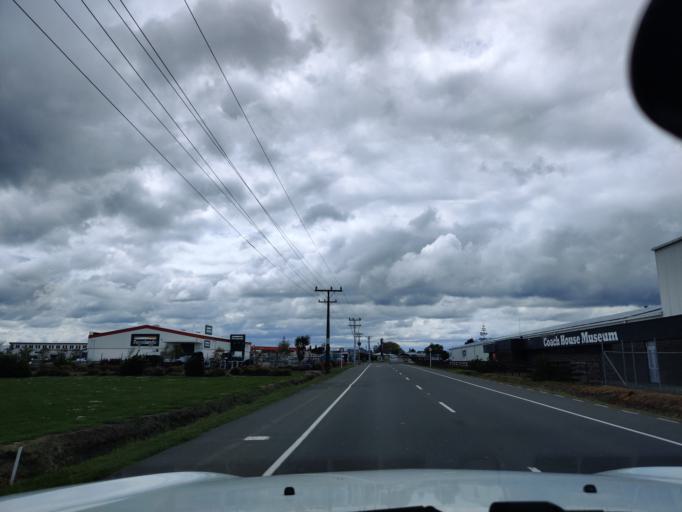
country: NZ
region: Manawatu-Wanganui
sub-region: Palmerston North City
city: Palmerston North
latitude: -40.2322
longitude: 175.5665
